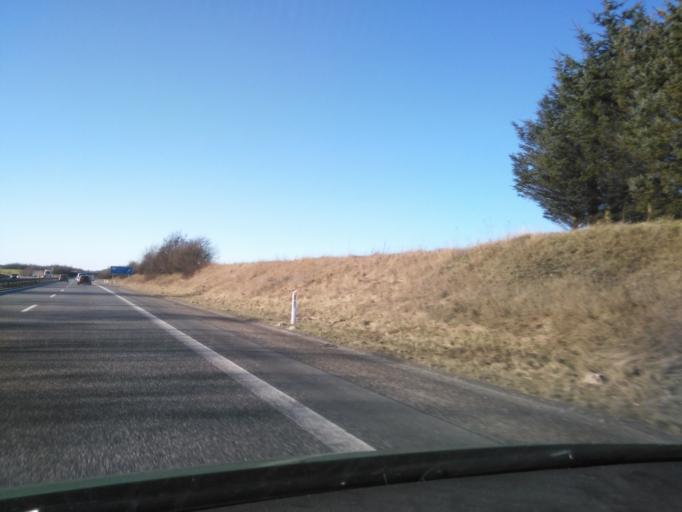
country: DK
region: North Denmark
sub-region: Mariagerfjord Kommune
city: Mariager
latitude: 56.5399
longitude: 9.9099
